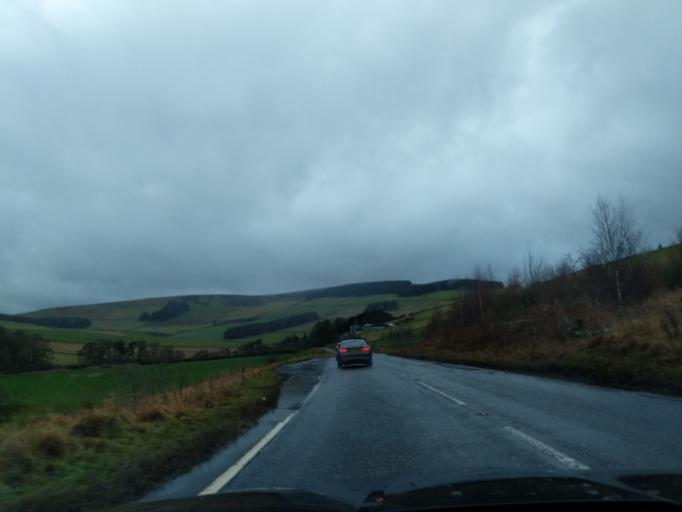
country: GB
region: Scotland
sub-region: The Scottish Borders
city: Galashiels
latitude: 55.6646
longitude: -2.8648
